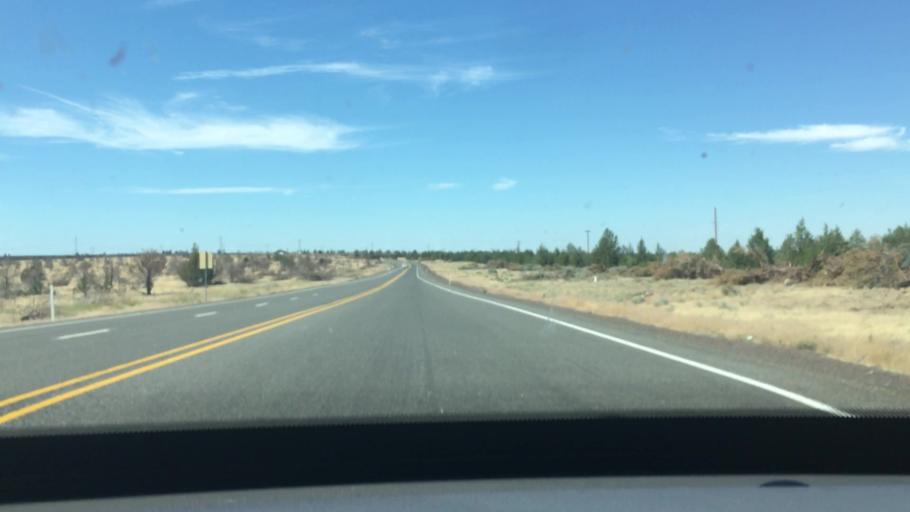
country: US
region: Oregon
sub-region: Jefferson County
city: Madras
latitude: 44.9066
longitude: -120.9390
